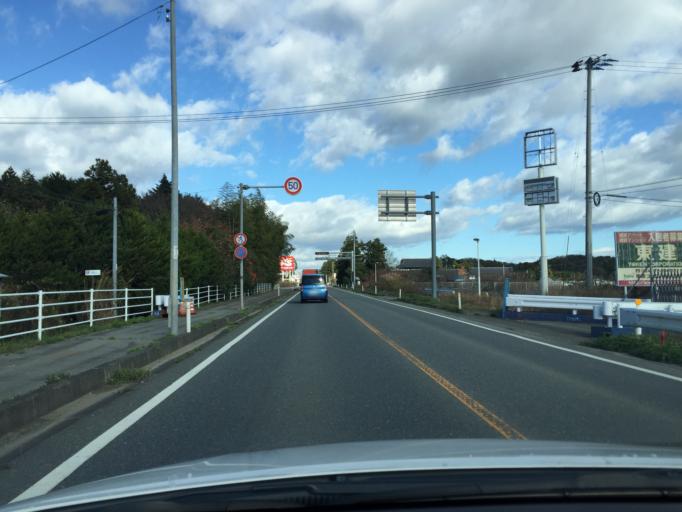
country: JP
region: Fukushima
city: Namie
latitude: 37.3623
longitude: 141.0096
